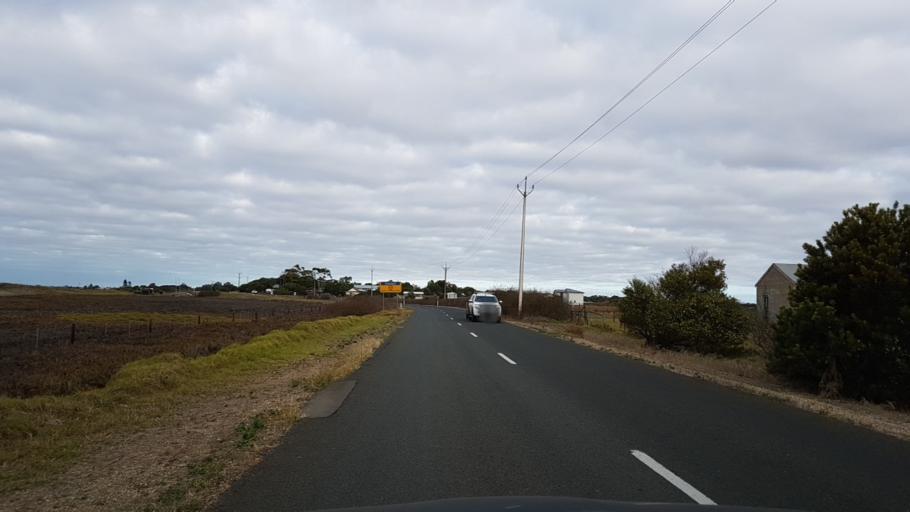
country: AU
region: South Australia
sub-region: Alexandrina
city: Langhorne Creek
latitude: -35.3998
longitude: 138.9852
